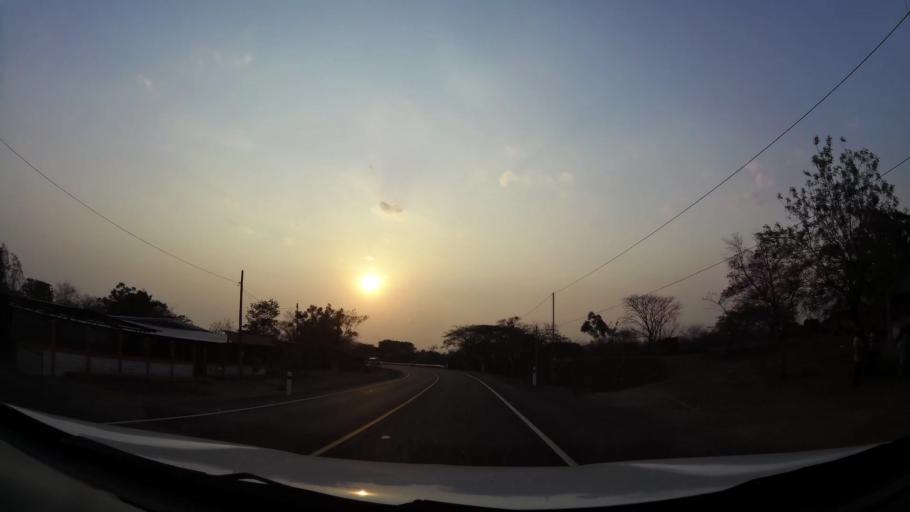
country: NI
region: Leon
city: La Paz Centro
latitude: 12.3375
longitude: -86.6595
